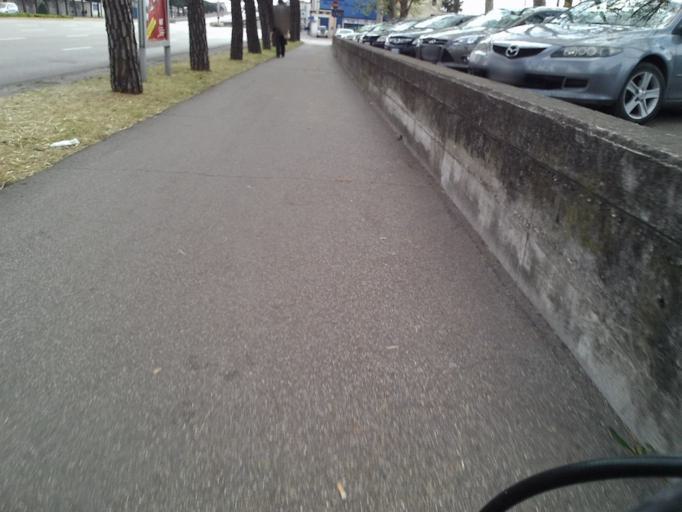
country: IT
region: Veneto
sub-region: Provincia di Verona
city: Verona
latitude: 45.4266
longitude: 10.9854
